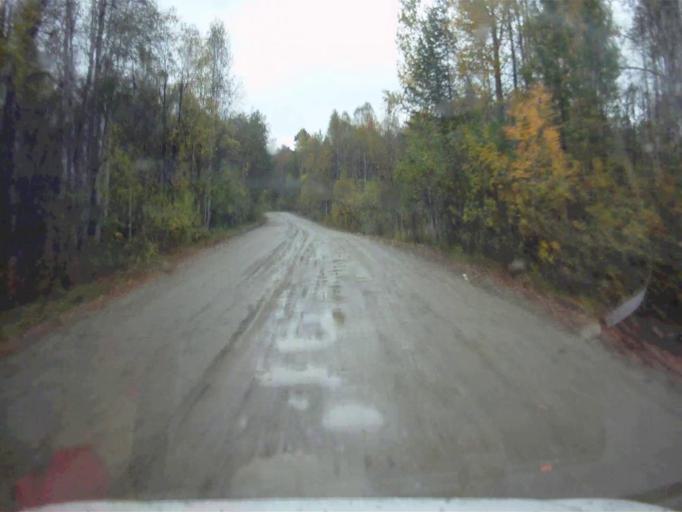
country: RU
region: Chelyabinsk
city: Kyshtym
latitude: 55.8309
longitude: 60.4864
